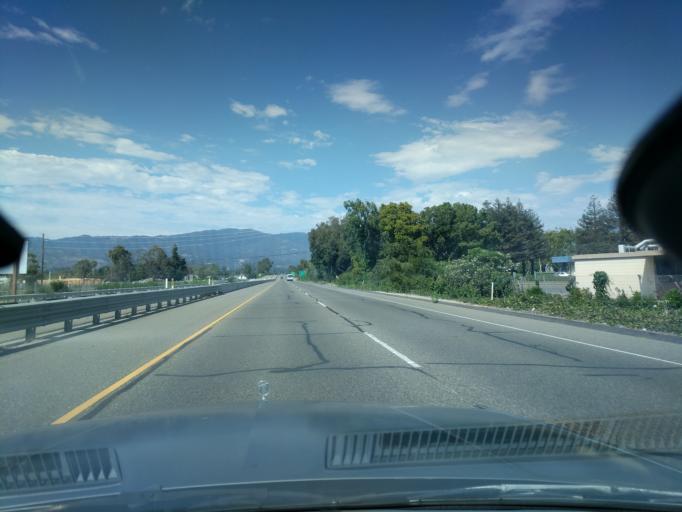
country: US
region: California
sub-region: Santa Barbara County
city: Goleta
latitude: 34.4294
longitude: -119.8227
